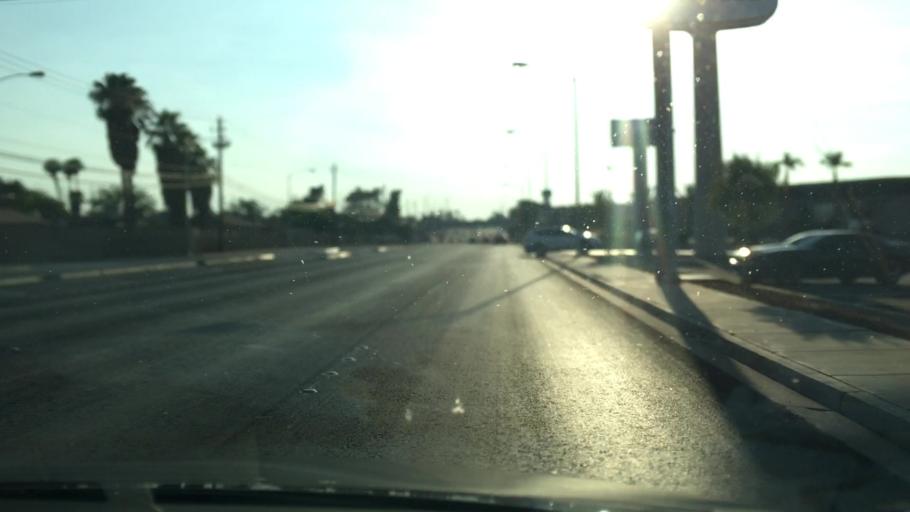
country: US
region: Nevada
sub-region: Clark County
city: Whitney
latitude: 36.1004
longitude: -115.0773
